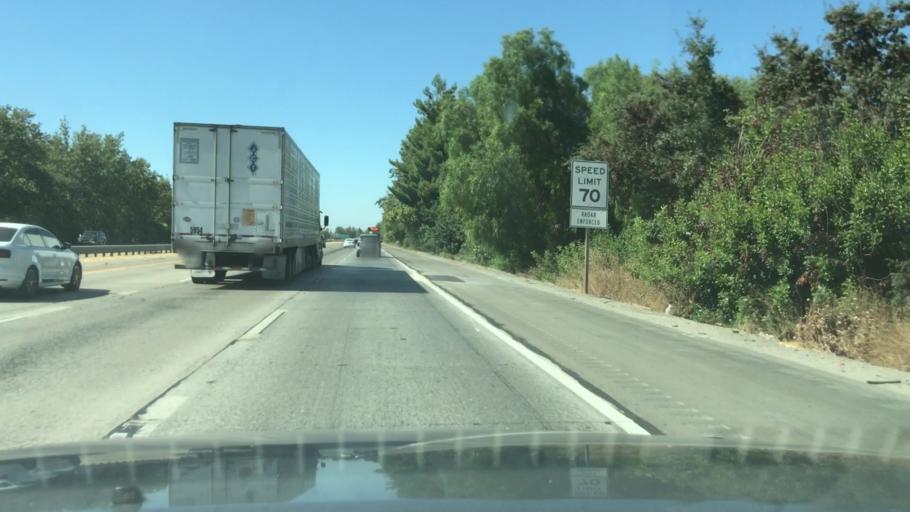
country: US
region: California
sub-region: San Joaquin County
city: Lincoln Village
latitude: 38.0279
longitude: -121.3619
